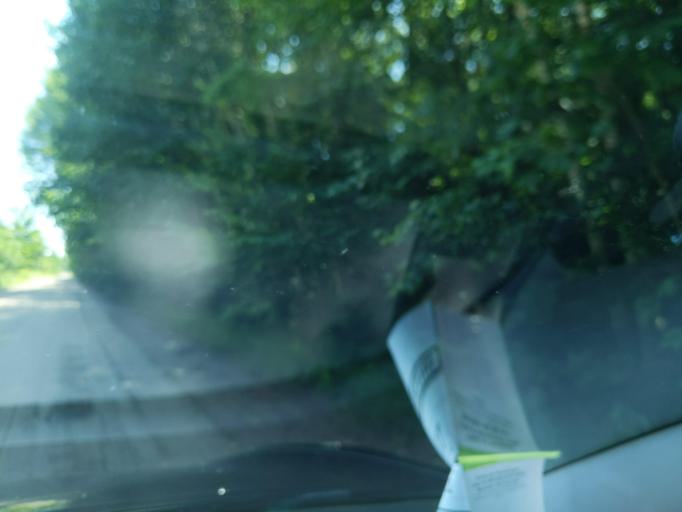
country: US
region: Michigan
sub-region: Cheboygan County
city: Cheboygan
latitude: 45.6792
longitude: -84.6660
